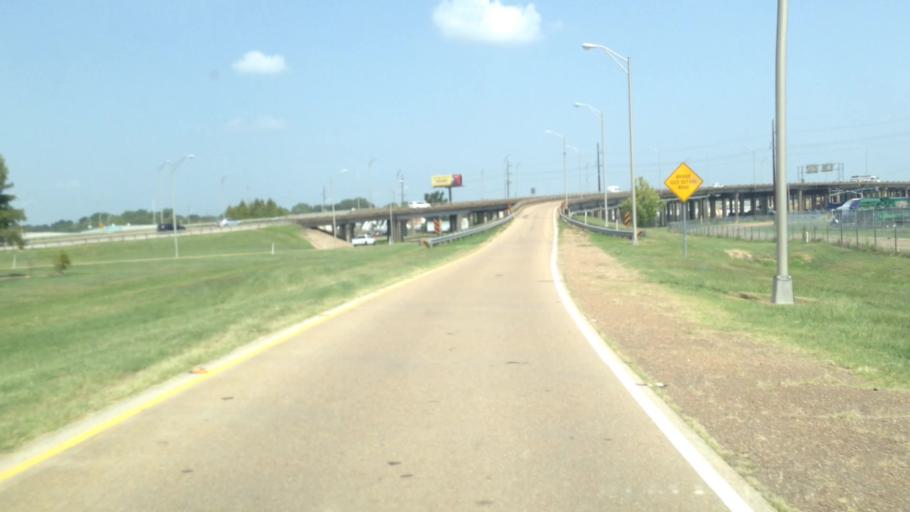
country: US
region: Louisiana
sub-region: Ouachita Parish
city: Monroe
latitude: 32.5000
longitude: -92.0811
